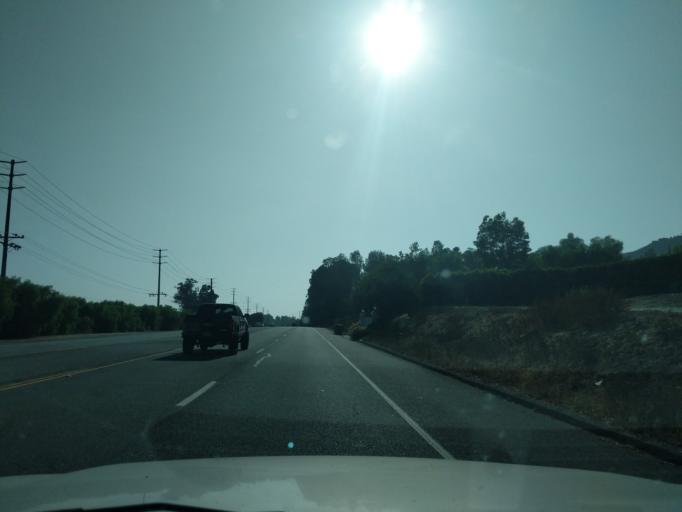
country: US
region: California
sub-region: Ventura County
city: Simi Valley
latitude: 34.2710
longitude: -118.8283
